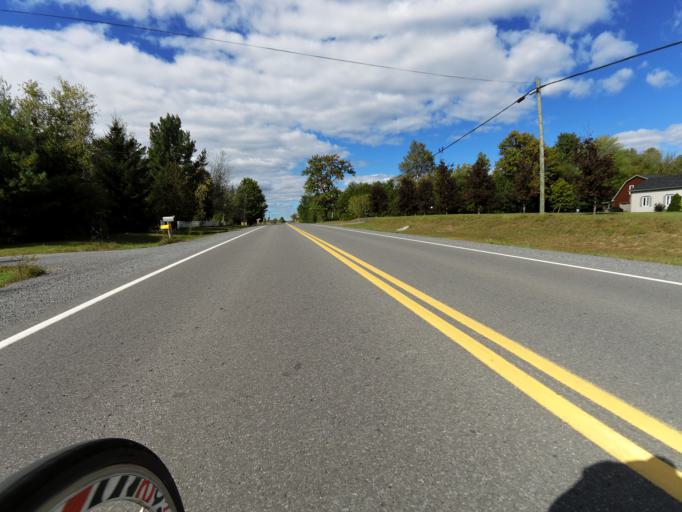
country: CA
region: Ontario
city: Bells Corners
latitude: 45.1885
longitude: -75.6787
